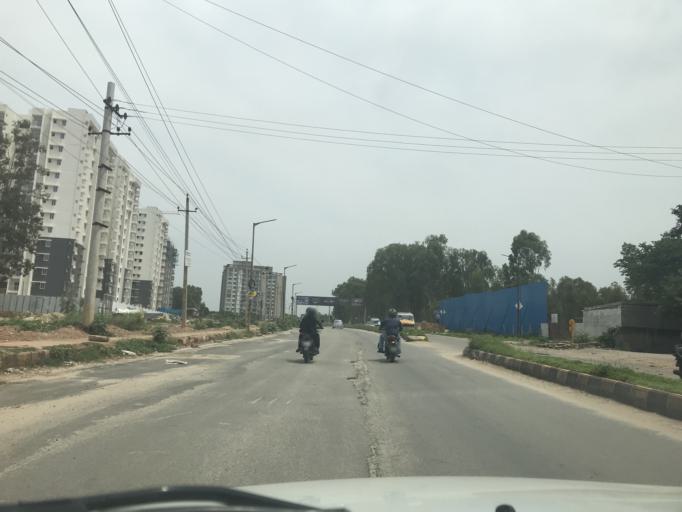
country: IN
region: Karnataka
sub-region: Bangalore Urban
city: Yelahanka
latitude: 13.0871
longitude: 77.6548
